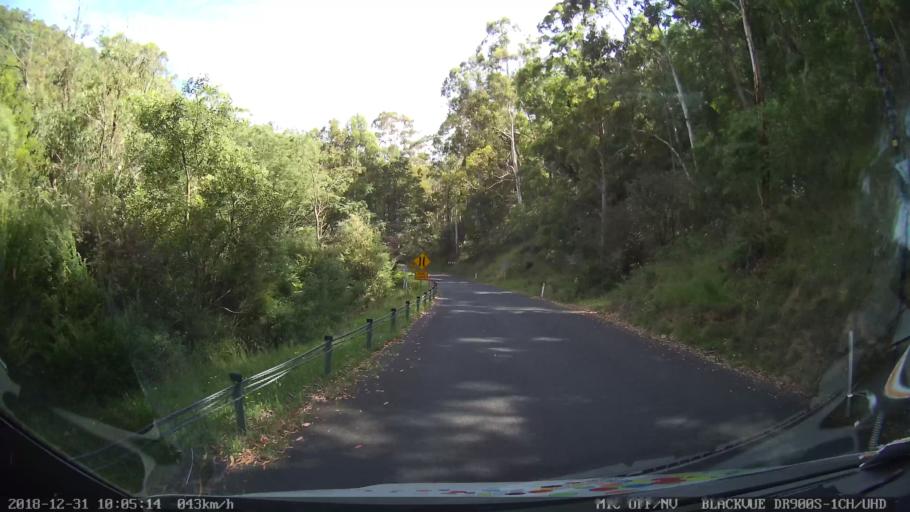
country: AU
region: New South Wales
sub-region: Snowy River
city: Jindabyne
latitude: -36.5272
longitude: 148.1939
